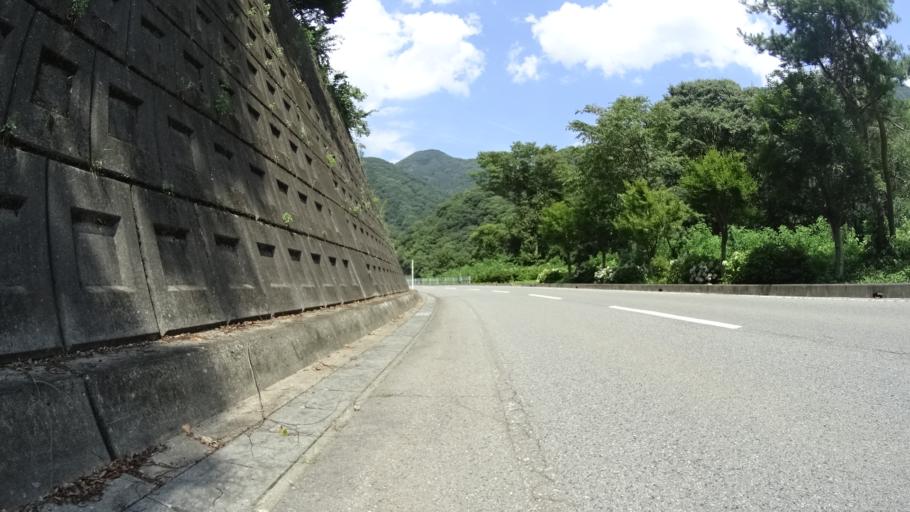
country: JP
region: Gunma
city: Tomioka
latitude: 36.0820
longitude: 138.7734
